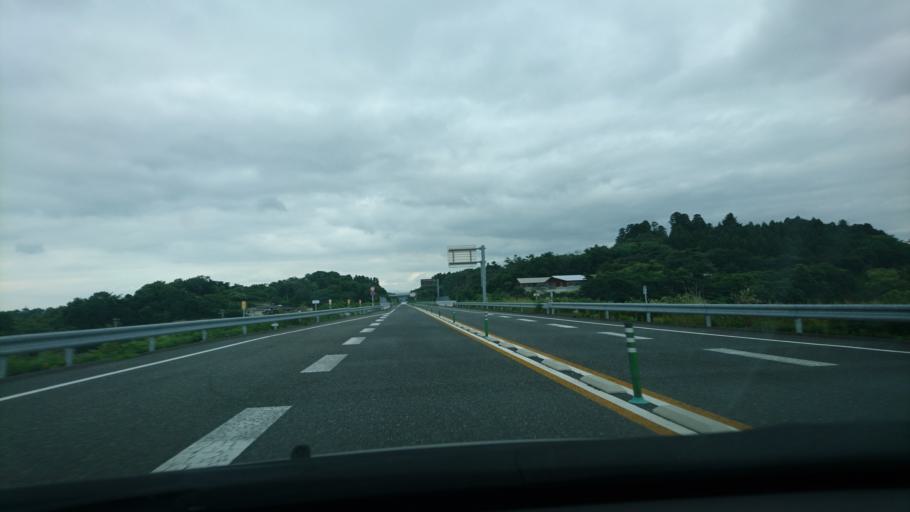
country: JP
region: Miyagi
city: Kogota
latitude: 38.7315
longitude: 141.0864
